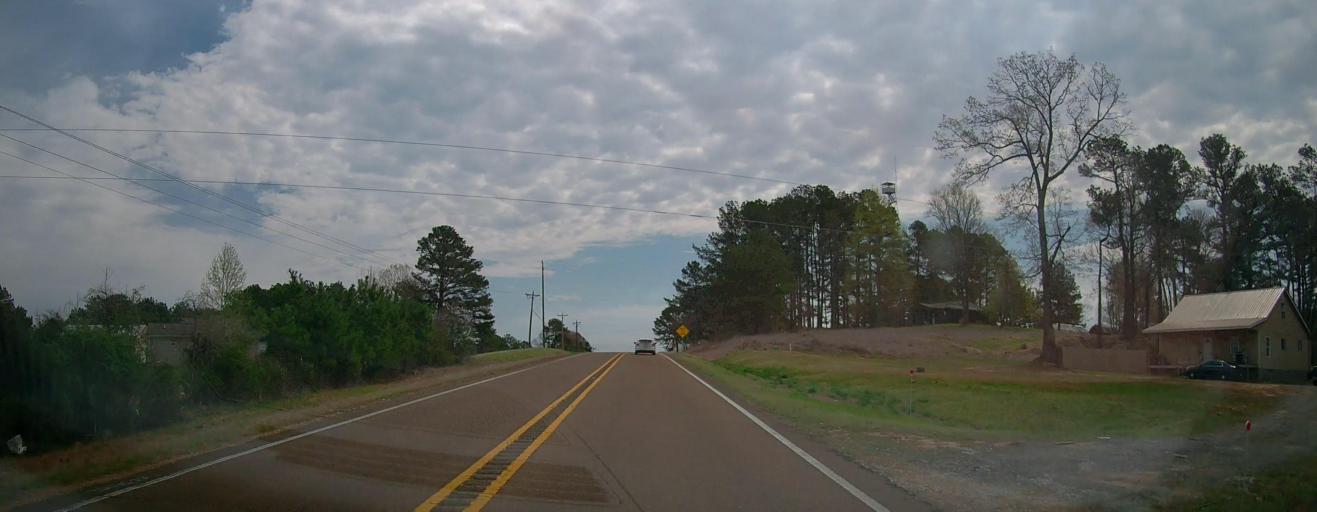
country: US
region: Mississippi
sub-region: Marshall County
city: Holly Springs
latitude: 34.8167
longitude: -89.5308
